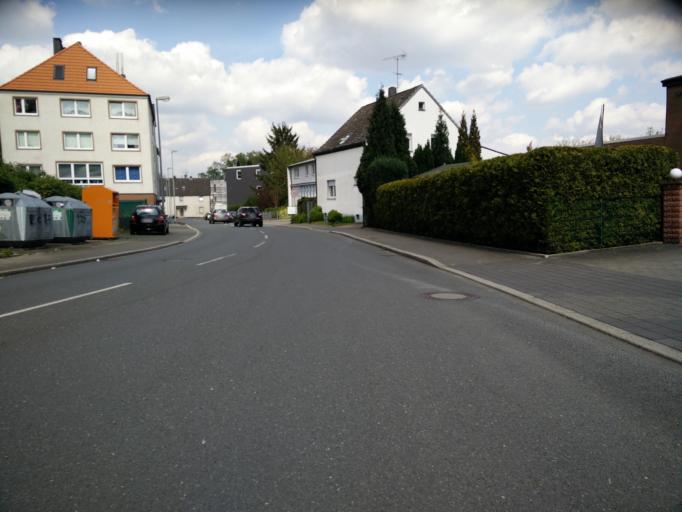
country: DE
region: North Rhine-Westphalia
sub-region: Regierungsbezirk Arnsberg
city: Herne
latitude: 51.5125
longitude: 7.2076
